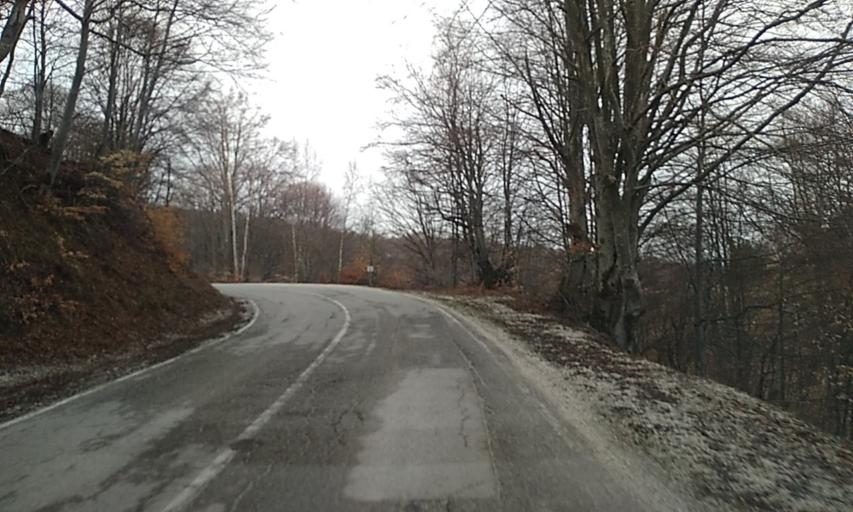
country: RS
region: Central Serbia
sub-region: Jablanicki Okrug
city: Crna Trava
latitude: 42.6816
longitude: 22.3655
